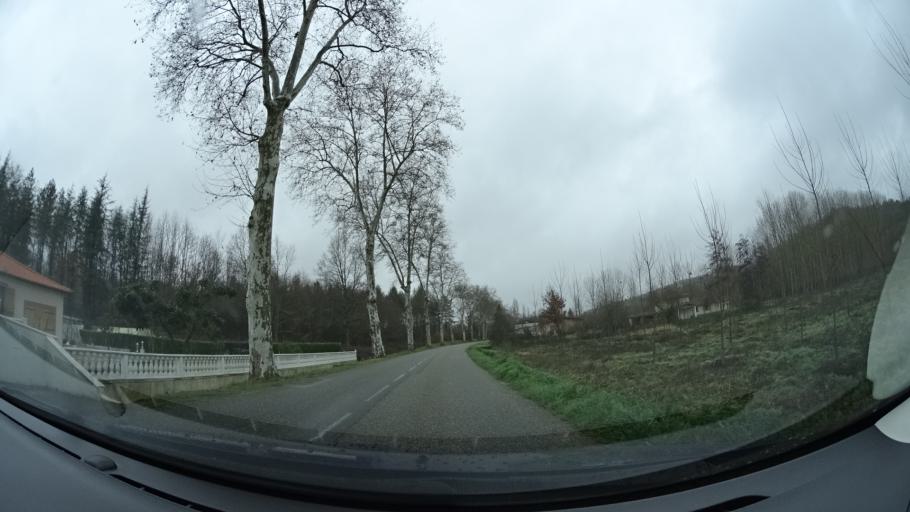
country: FR
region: Midi-Pyrenees
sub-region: Departement du Tarn-et-Garonne
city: Moissac
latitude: 44.1472
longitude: 1.1006
